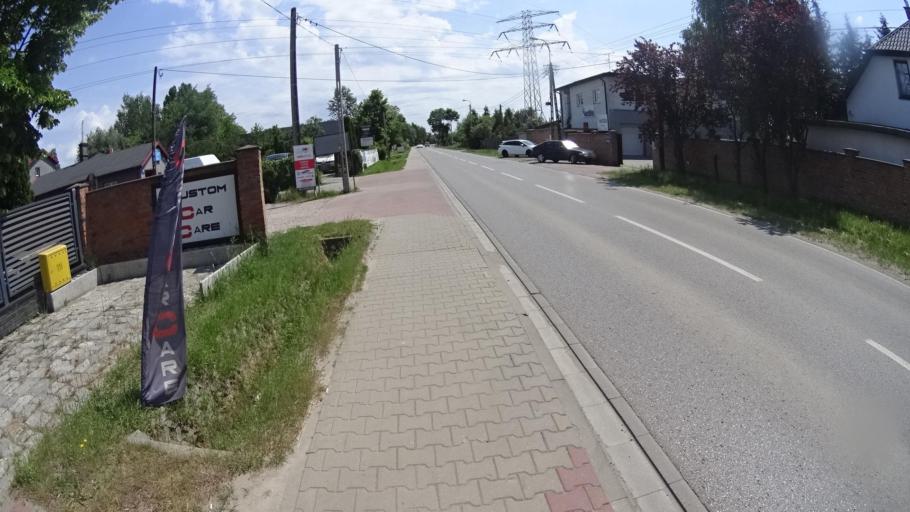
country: PL
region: Masovian Voivodeship
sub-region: Powiat warszawski zachodni
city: Stare Babice
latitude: 52.2593
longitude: 20.8347
